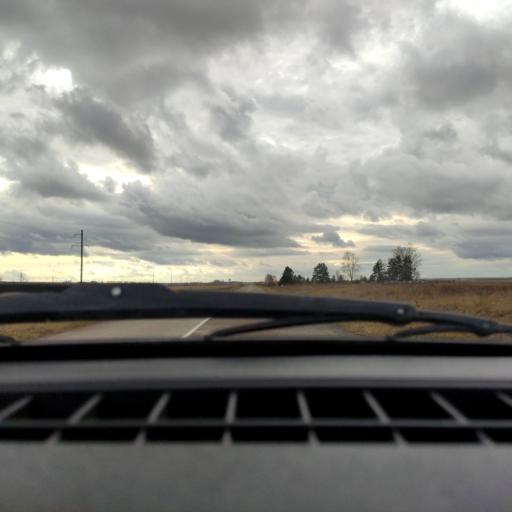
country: RU
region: Bashkortostan
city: Asanovo
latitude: 54.9278
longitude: 55.5175
